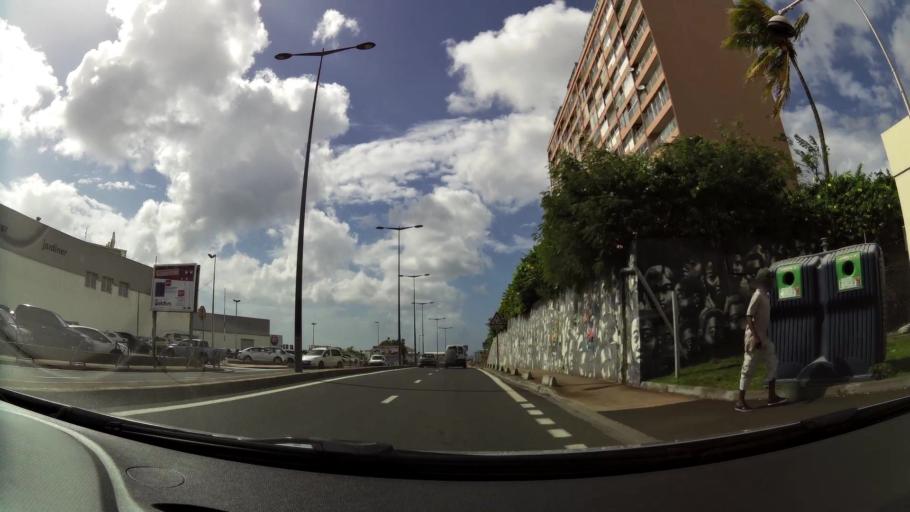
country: MQ
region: Martinique
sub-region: Martinique
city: Fort-de-France
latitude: 14.6050
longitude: -61.0862
